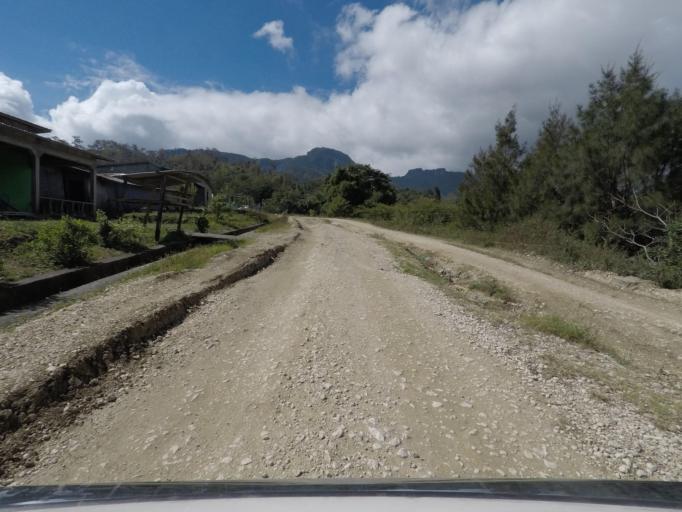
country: TL
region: Baucau
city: Venilale
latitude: -8.6771
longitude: 126.3712
